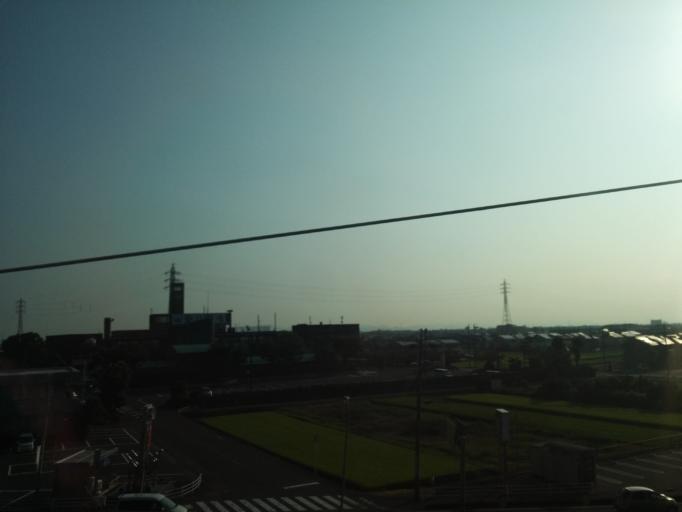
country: JP
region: Gifu
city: Ogaki
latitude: 35.3345
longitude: 136.6636
